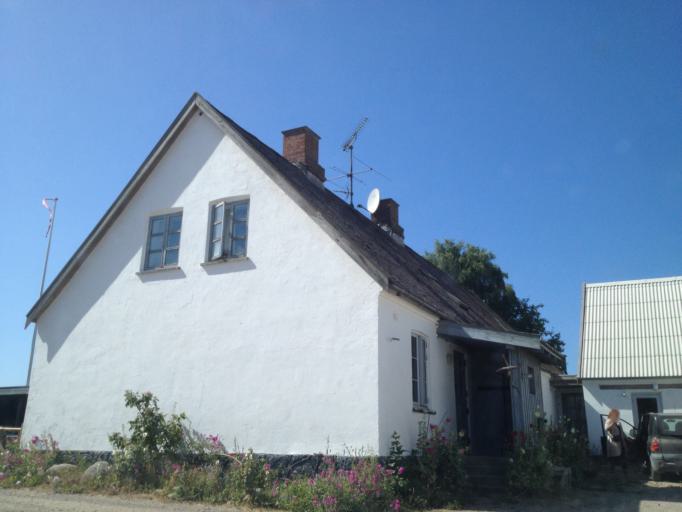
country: DK
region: Capital Region
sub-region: Fredensborg Kommune
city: Humlebaek
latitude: 56.0119
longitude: 12.4820
